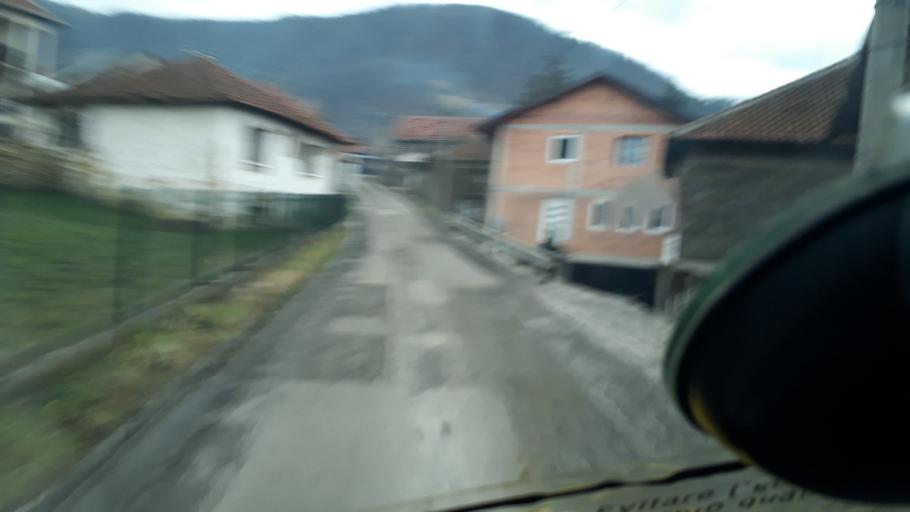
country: BA
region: Federation of Bosnia and Herzegovina
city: Zenica
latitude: 44.1536
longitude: 17.9721
